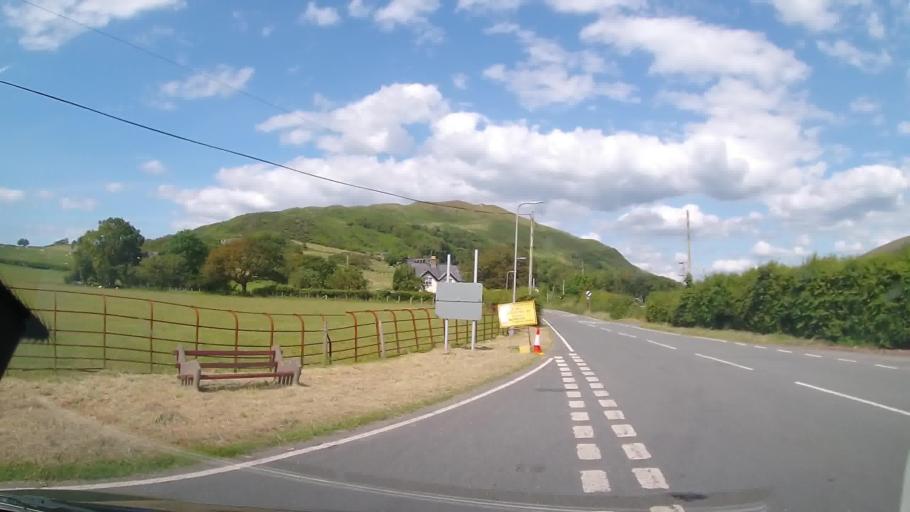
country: GB
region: Wales
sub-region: Gwynedd
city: Tywyn
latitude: 52.6082
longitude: -4.0479
